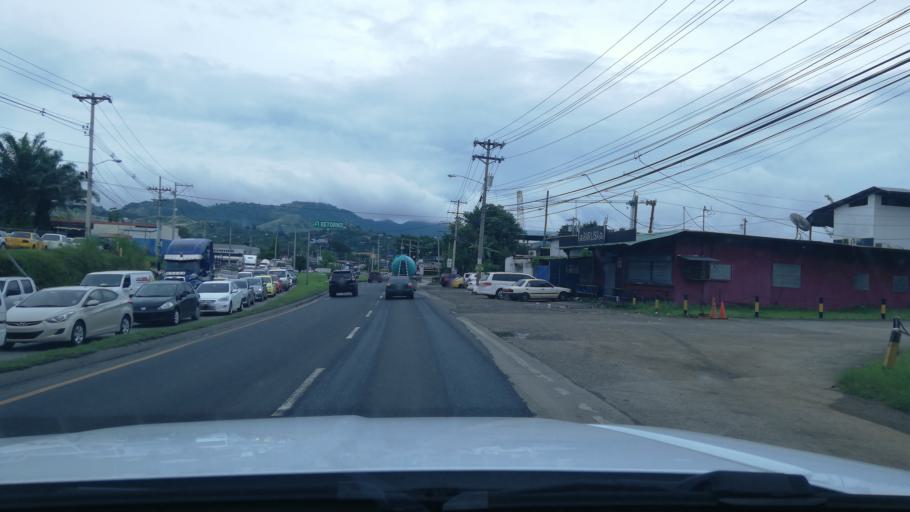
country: PA
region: Panama
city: Las Cumbres
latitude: 9.0699
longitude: -79.5196
